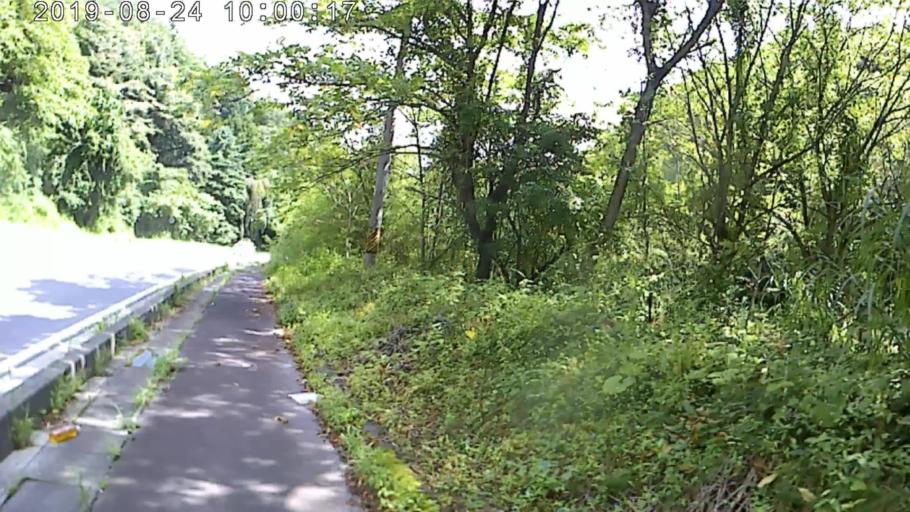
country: JP
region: Nagano
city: Kamimaruko
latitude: 36.2595
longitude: 138.2888
